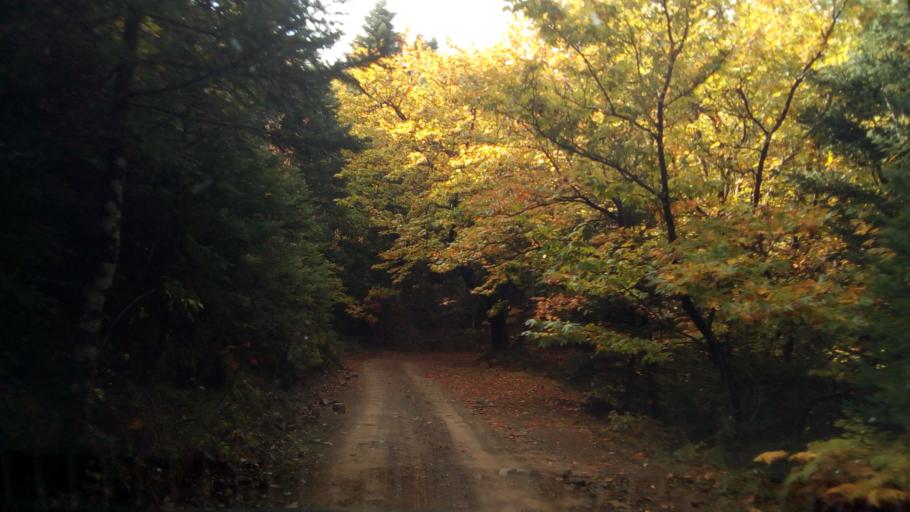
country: GR
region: Central Greece
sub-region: Nomos Fokidos
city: Lidoriki
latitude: 38.4815
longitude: 22.0558
